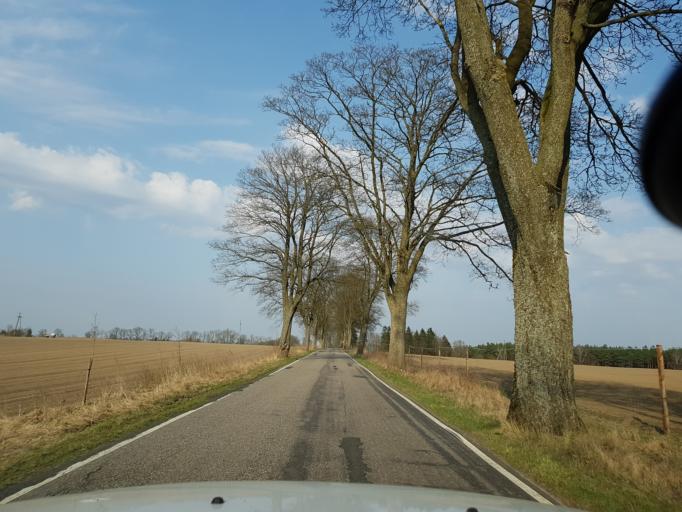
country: PL
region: West Pomeranian Voivodeship
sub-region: Powiat drawski
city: Drawsko Pomorskie
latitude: 53.5950
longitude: 15.8998
